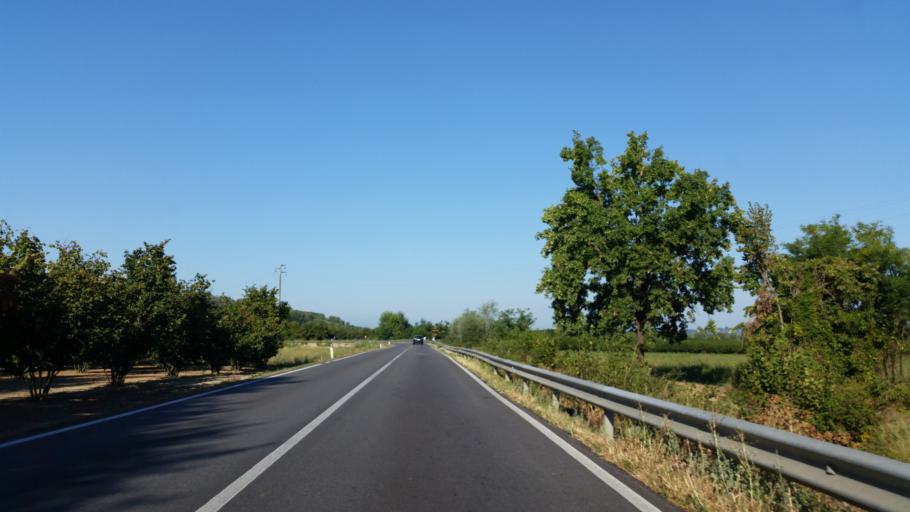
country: IT
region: Piedmont
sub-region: Provincia di Cuneo
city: Santa Vittoria d'Alba
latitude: 44.6840
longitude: 7.9521
